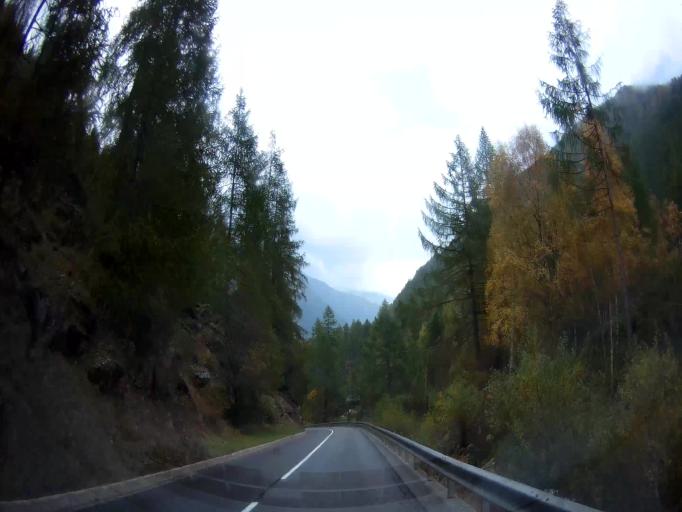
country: IT
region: Trentino-Alto Adige
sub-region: Bolzano
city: Senales
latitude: 46.7153
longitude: 10.8746
